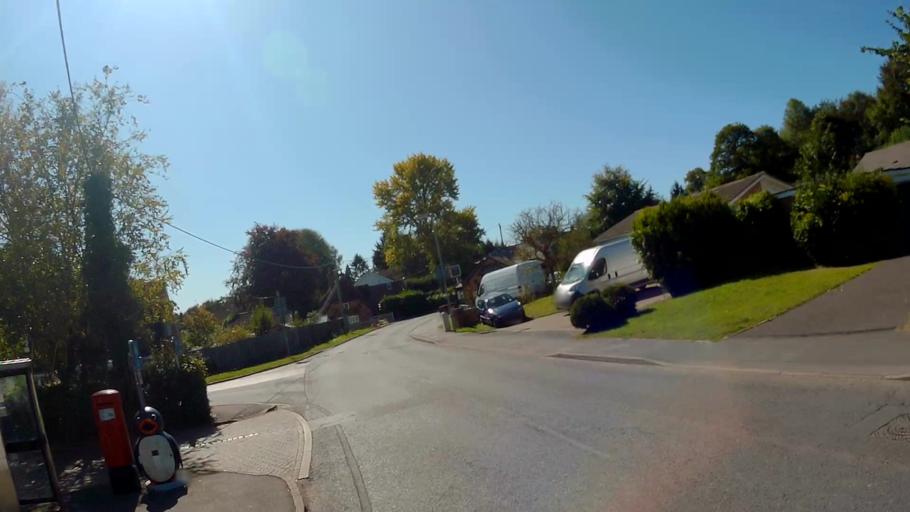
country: GB
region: England
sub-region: Hampshire
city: Overton
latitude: 51.2487
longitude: -1.1786
